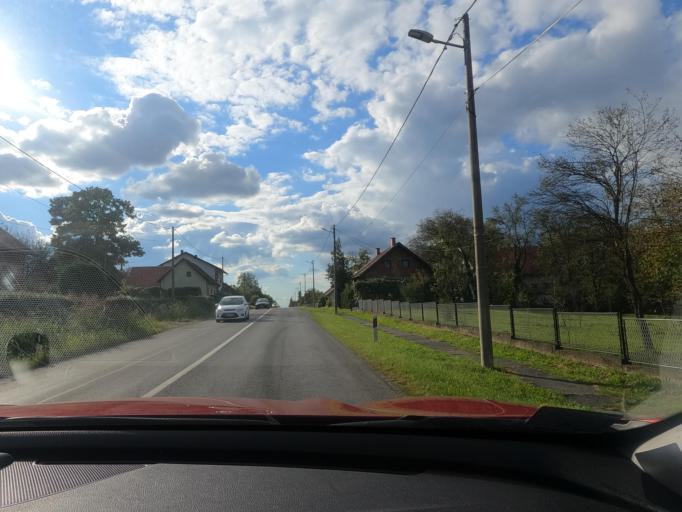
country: HR
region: Sisacko-Moslavacka
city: Petrinja
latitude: 45.4430
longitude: 16.3252
